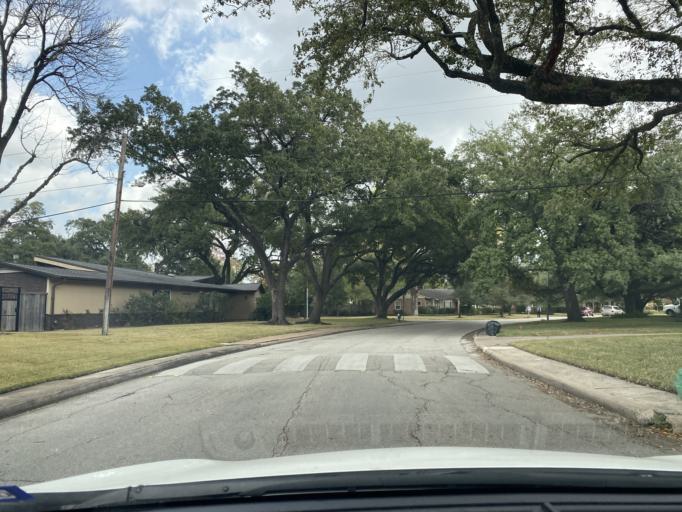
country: US
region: Texas
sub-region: Harris County
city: Hunters Creek Village
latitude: 29.7463
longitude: -95.4692
